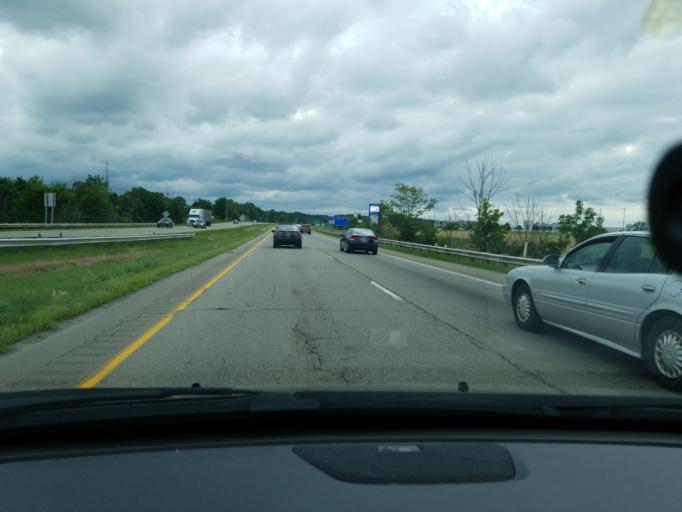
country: US
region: Ohio
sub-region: Lorain County
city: Amherst
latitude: 41.4116
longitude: -82.2279
